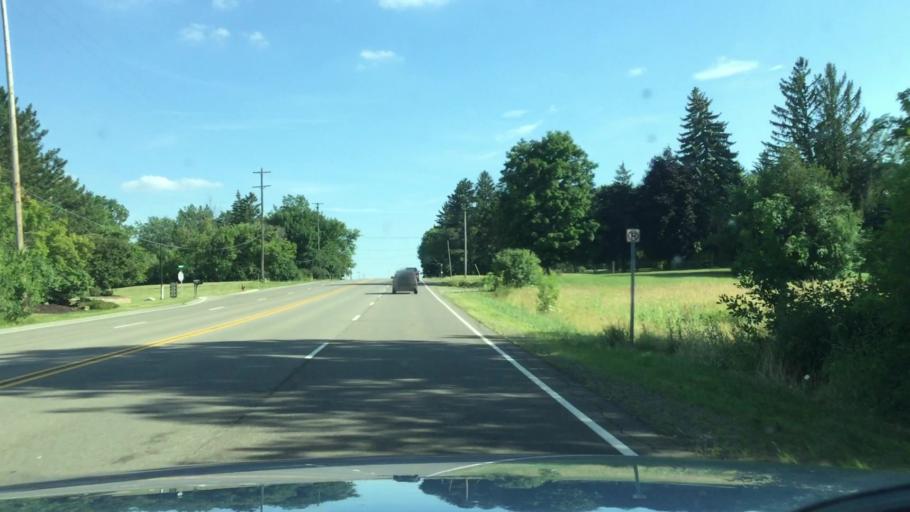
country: US
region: Michigan
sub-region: Genesee County
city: Grand Blanc
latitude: 42.8988
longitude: -83.6018
